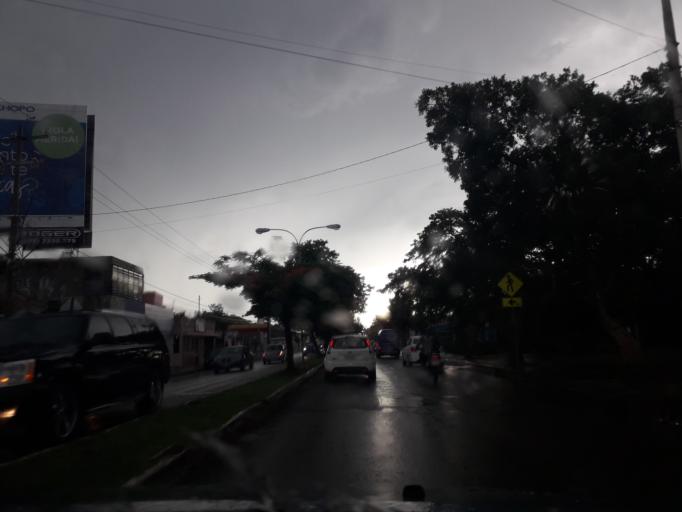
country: MX
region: Yucatan
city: Merida
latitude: 20.9800
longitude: -89.6478
